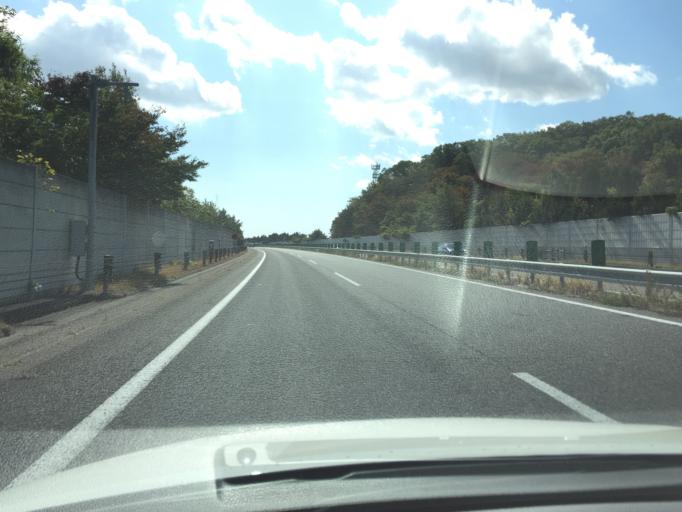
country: JP
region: Fukushima
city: Koriyama
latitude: 37.3961
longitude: 140.3105
